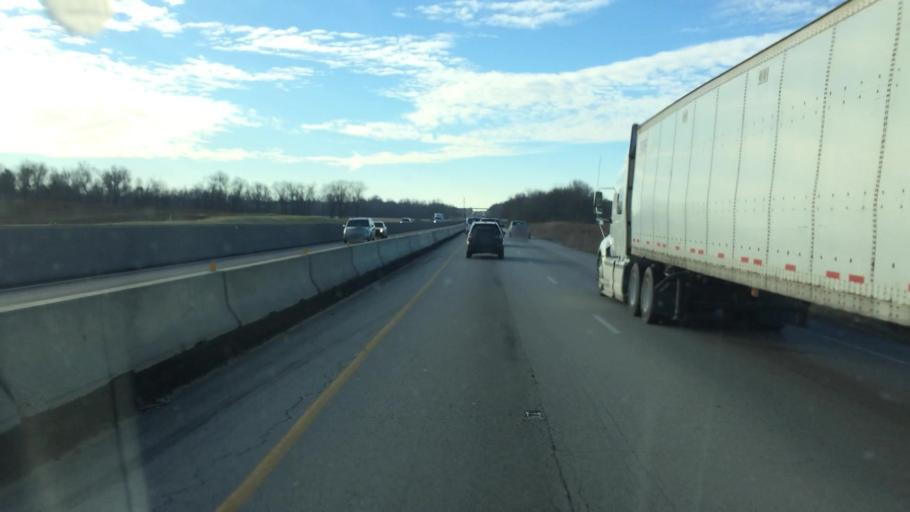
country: US
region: Kentucky
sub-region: Hardin County
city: Elizabethtown
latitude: 37.5720
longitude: -85.8741
